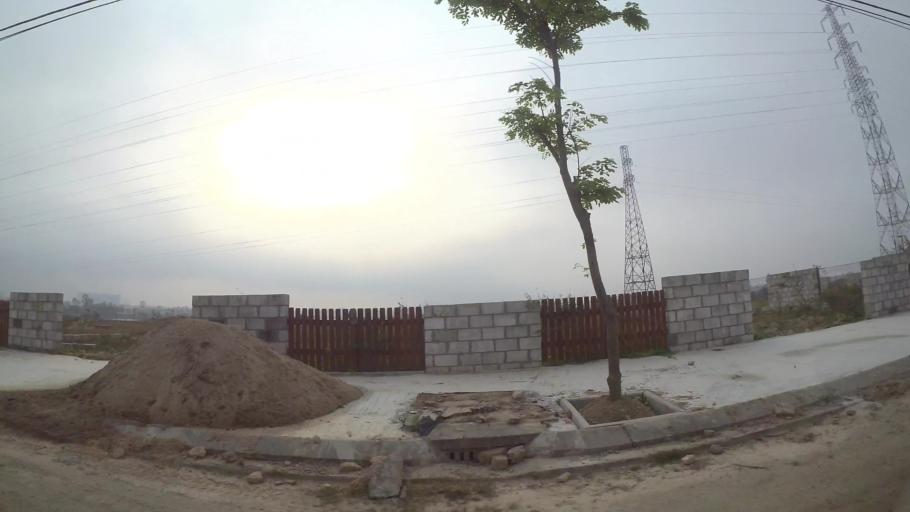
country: VN
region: Da Nang
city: Ngu Hanh Son
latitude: 16.0206
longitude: 108.2369
